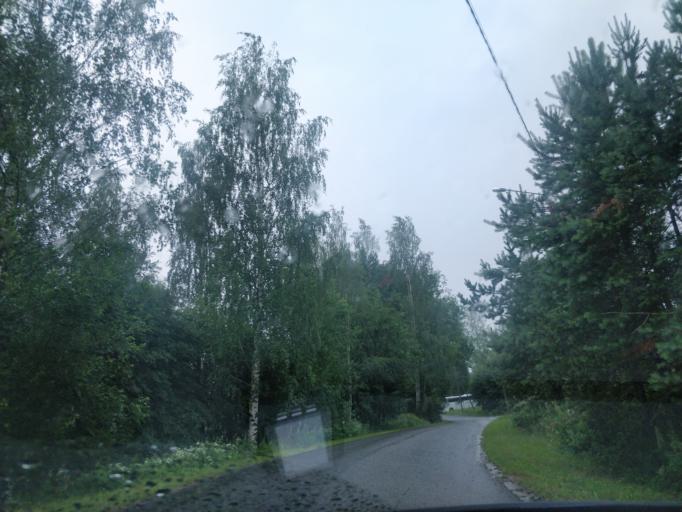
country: FI
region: Southern Savonia
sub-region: Mikkeli
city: Pertunmaa
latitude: 61.4258
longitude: 26.4253
